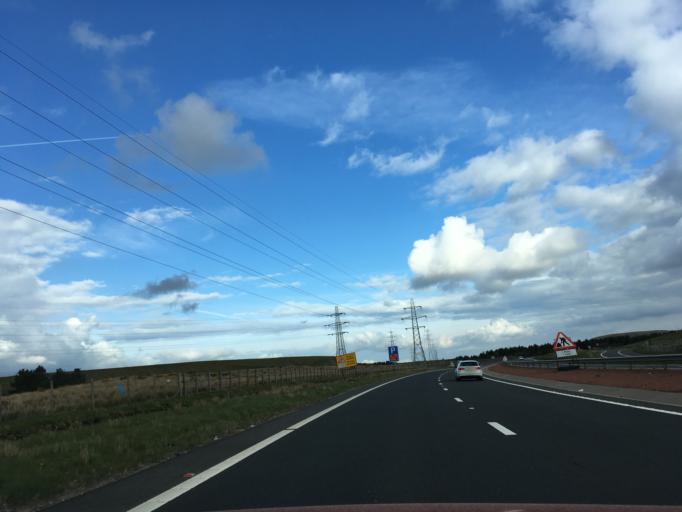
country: GB
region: Wales
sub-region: Blaenau Gwent
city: Brynmawr
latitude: 51.8080
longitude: -3.2060
